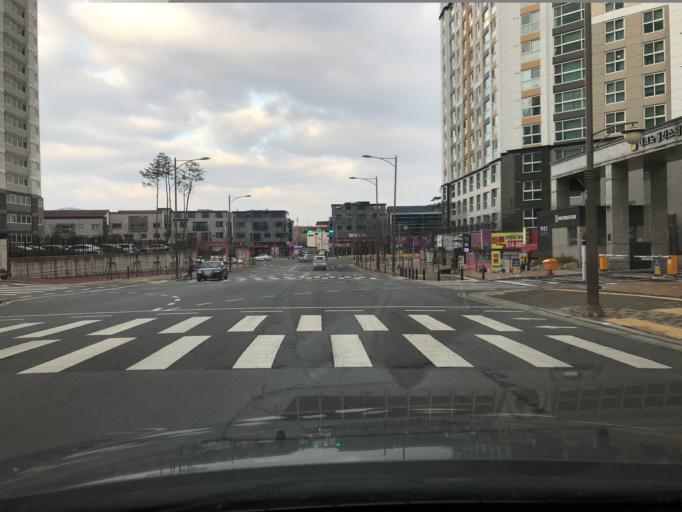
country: KR
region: Daegu
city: Hwawon
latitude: 35.6918
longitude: 128.4509
